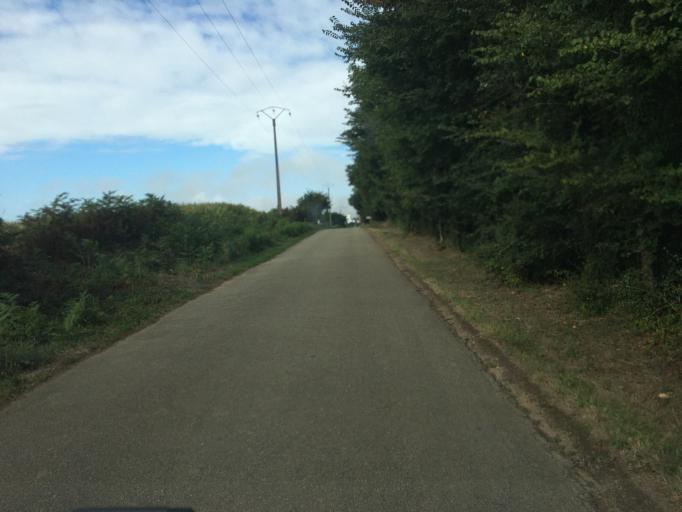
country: FR
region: Brittany
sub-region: Departement du Finistere
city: Beuzec-Cap-Sizun
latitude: 48.0750
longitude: -4.4974
